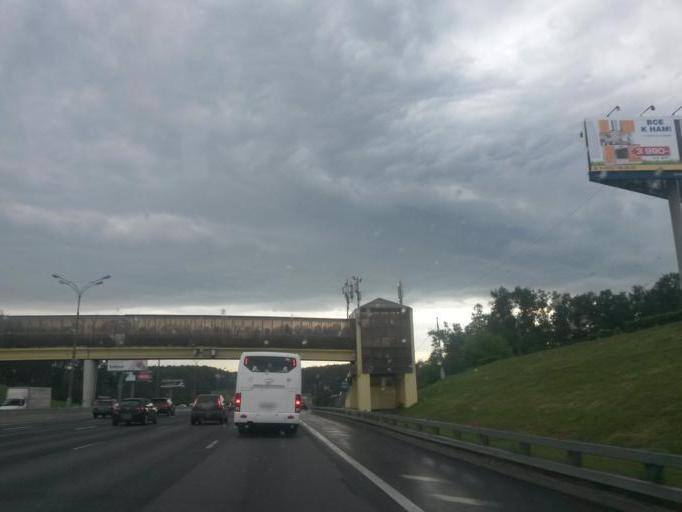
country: RU
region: Moscow
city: Zyablikovo
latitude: 55.6091
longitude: 37.7661
